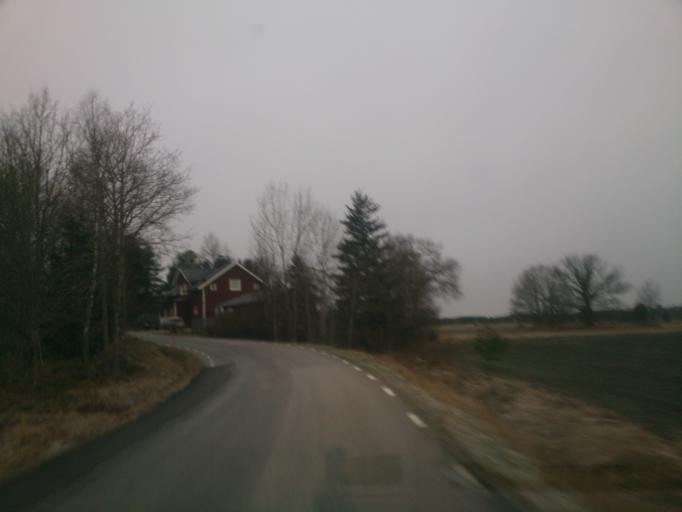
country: SE
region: OEstergoetland
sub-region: Norrkopings Kommun
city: Krokek
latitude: 58.5003
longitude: 16.5779
